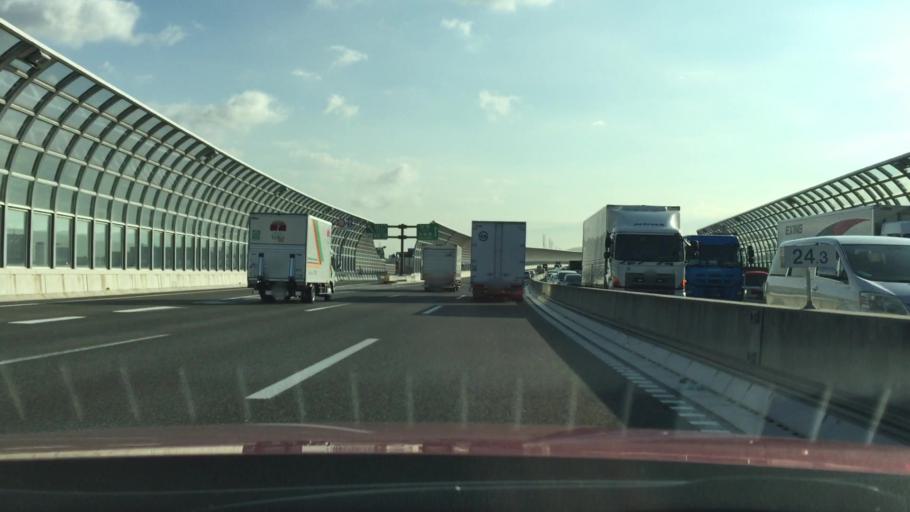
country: JP
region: Osaka
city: Neyagawa
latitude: 34.7427
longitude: 135.6184
